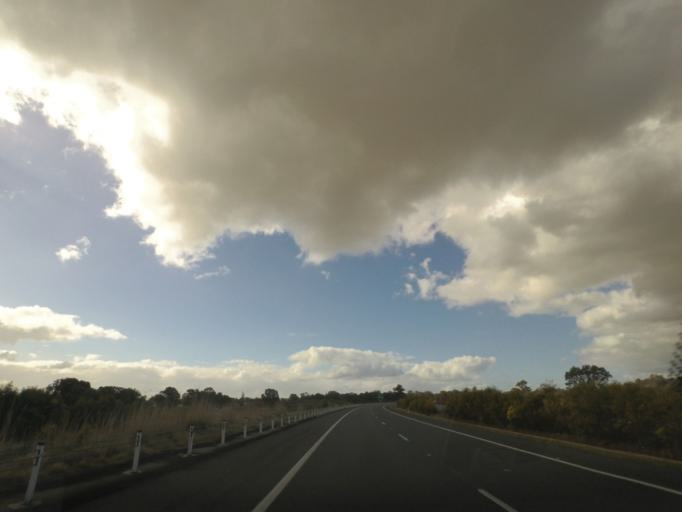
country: AU
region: New South Wales
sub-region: Greater Hume Shire
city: Holbrook
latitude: -35.7115
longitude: 147.3048
